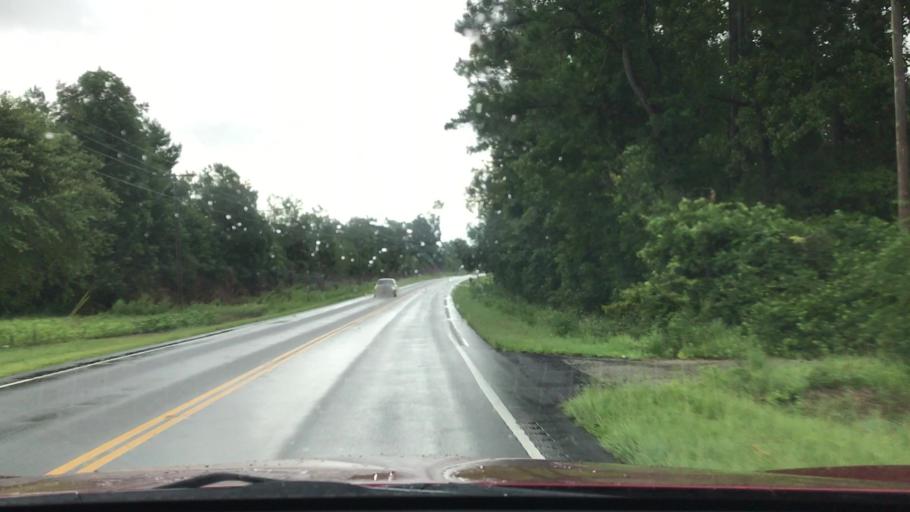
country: US
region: South Carolina
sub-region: Horry County
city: Loris
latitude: 33.9051
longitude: -78.8490
